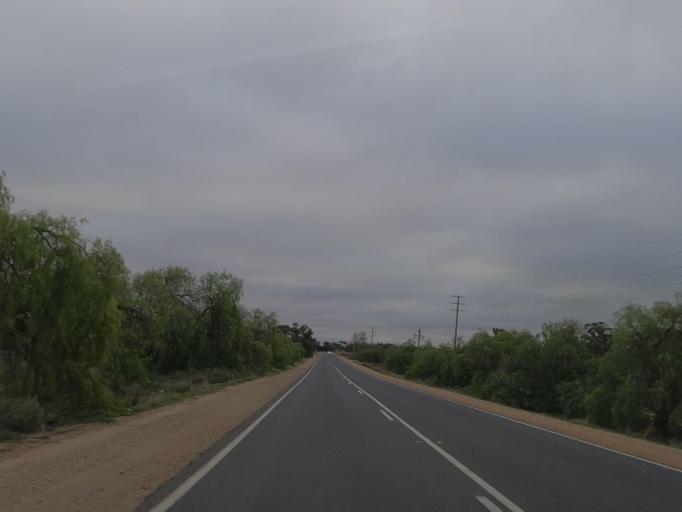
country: AU
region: Victoria
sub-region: Swan Hill
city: Swan Hill
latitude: -35.4449
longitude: 143.6190
